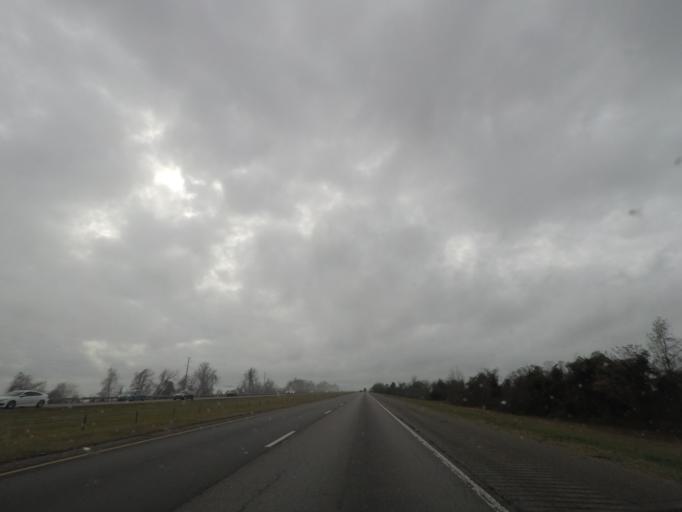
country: US
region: South Carolina
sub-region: Orangeburg County
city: Holly Hill
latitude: 33.5136
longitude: -80.4420
